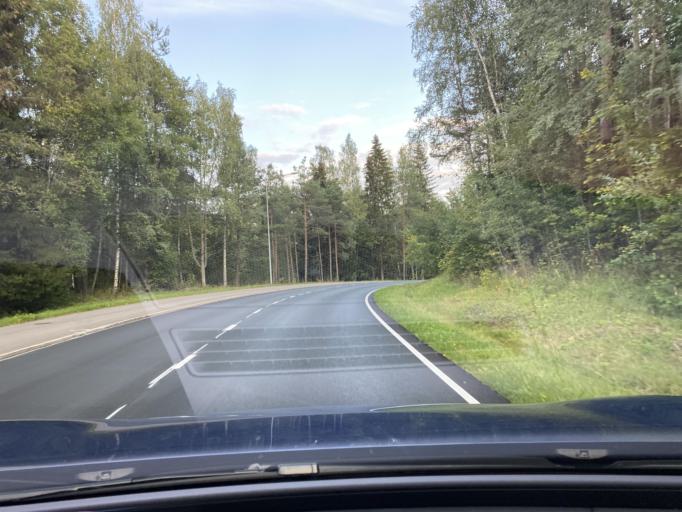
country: FI
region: Kymenlaakso
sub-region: Kouvola
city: Kouvola
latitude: 60.8987
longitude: 26.6534
